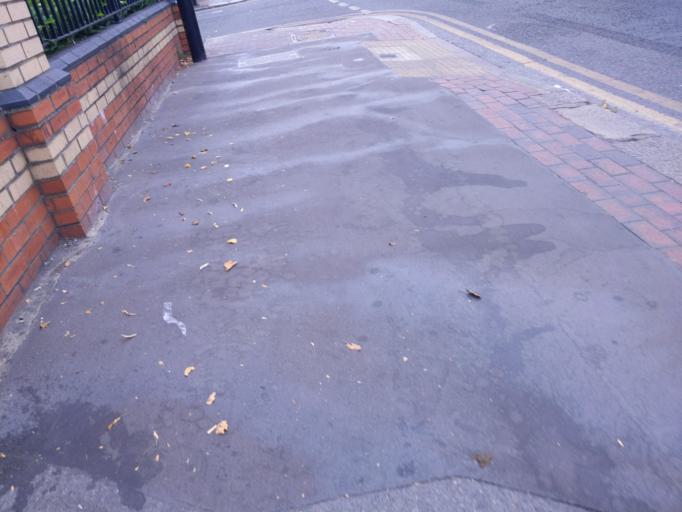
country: GB
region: England
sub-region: Greater London
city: Croydon
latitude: 51.3909
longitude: -0.1126
